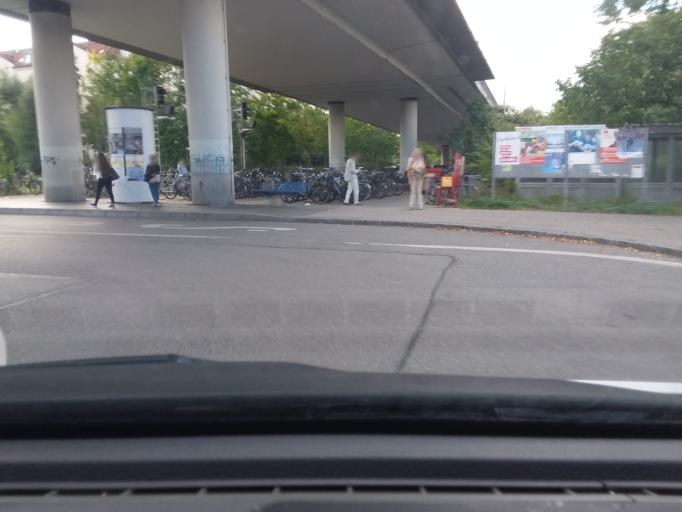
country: DE
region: Bavaria
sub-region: Upper Bavaria
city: Unterschleissheim
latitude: 48.2729
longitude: 11.5686
